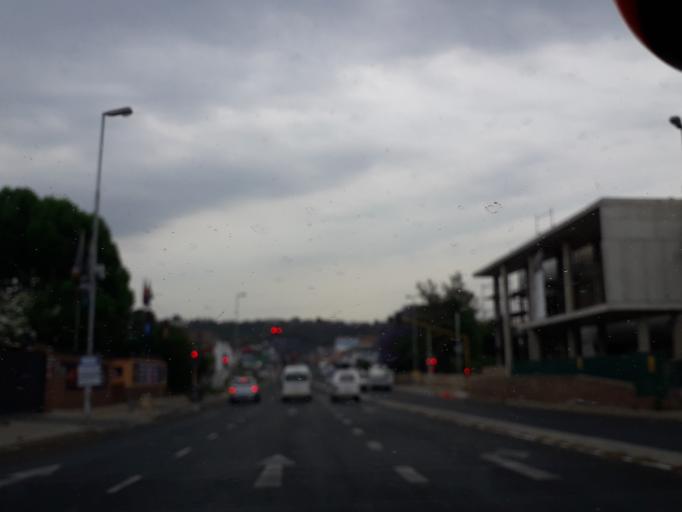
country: ZA
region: Gauteng
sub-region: City of Johannesburg Metropolitan Municipality
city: Johannesburg
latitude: -26.1541
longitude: 28.0859
